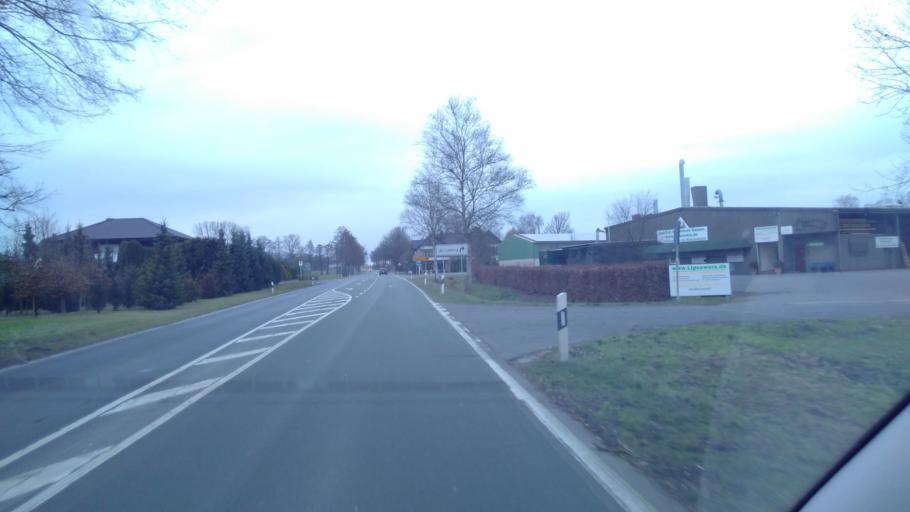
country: DE
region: North Rhine-Westphalia
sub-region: Regierungsbezirk Detmold
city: Delbruck
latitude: 51.8033
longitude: 8.5595
